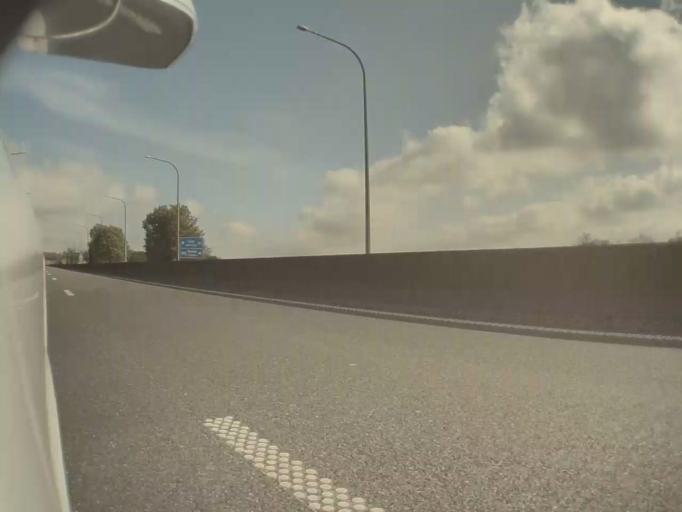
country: BE
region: Wallonia
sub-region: Province de Namur
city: Somme-Leuze
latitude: 50.2866
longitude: 5.3487
